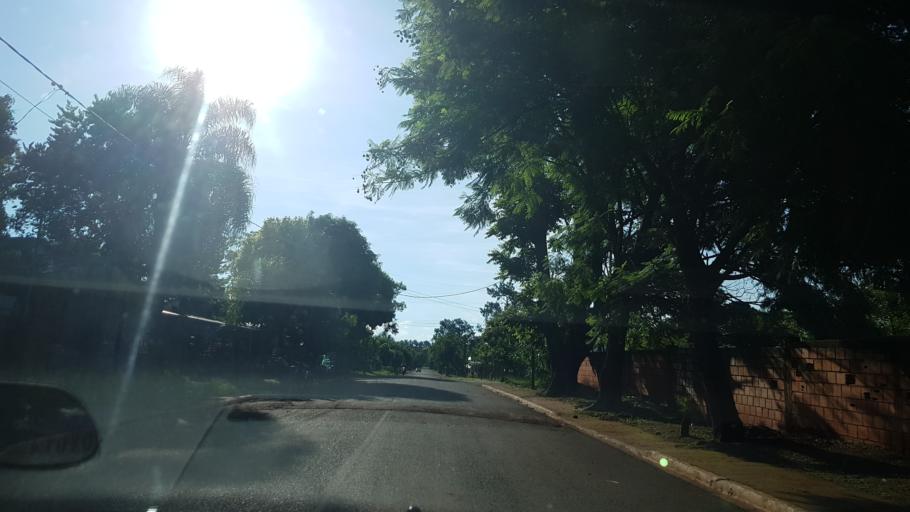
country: AR
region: Misiones
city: Puerto Libertad
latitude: -25.9230
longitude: -54.5843
